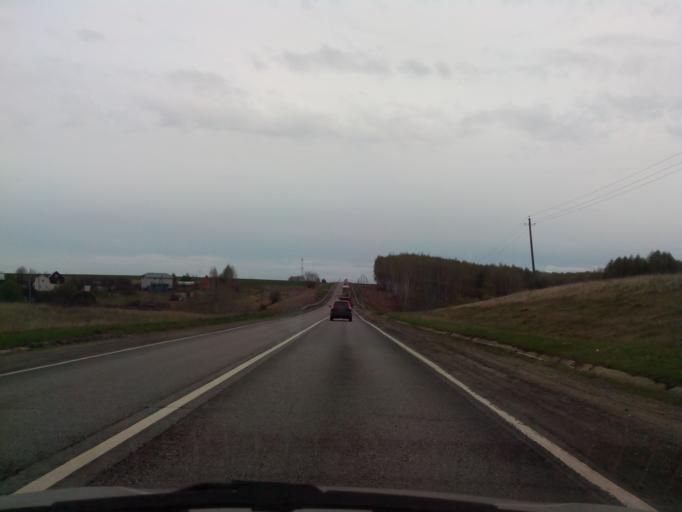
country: RU
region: Moskovskaya
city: Ozherel'ye
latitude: 54.7118
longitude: 38.2899
